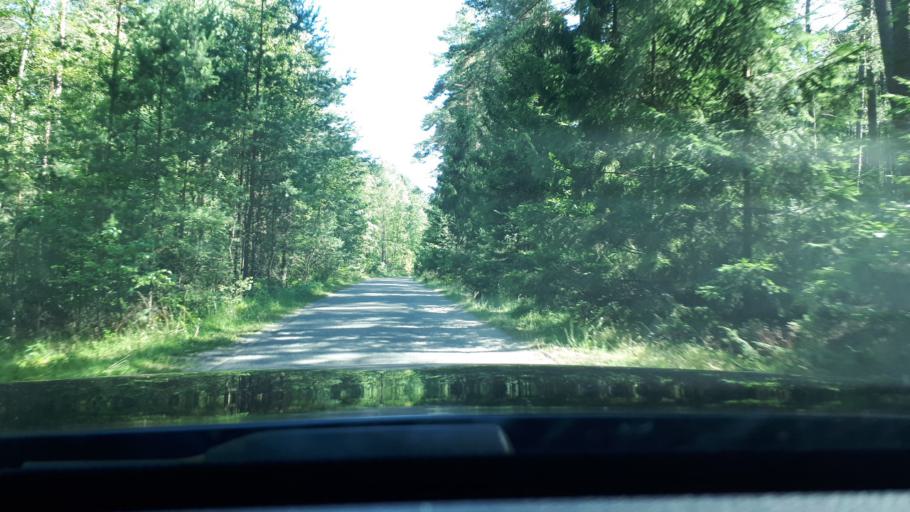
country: PL
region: Warmian-Masurian Voivodeship
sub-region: Powiat olsztynski
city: Stawiguda
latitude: 53.5800
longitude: 20.4529
